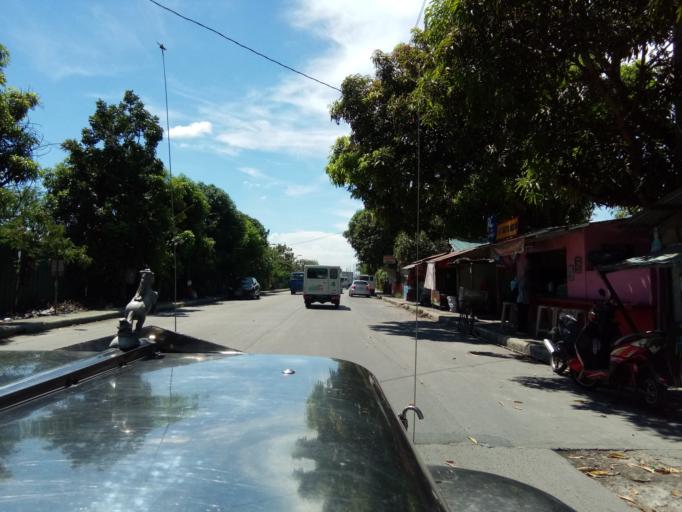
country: PH
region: Calabarzon
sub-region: Province of Cavite
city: General Trias
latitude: 14.3695
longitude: 120.8900
